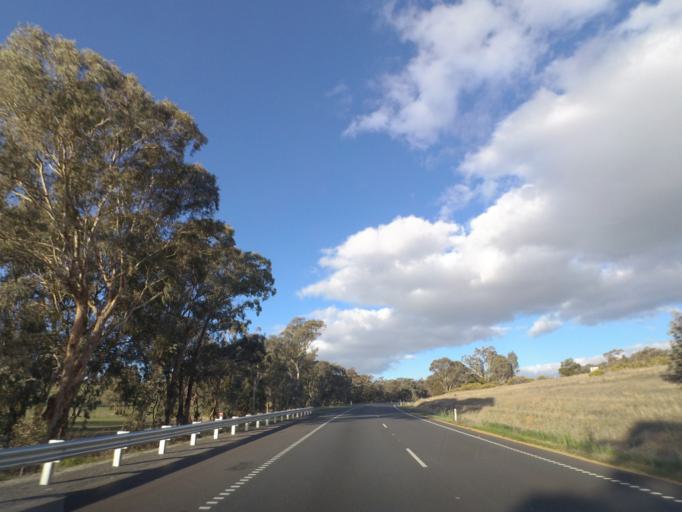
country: AU
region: New South Wales
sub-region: Gundagai
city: Gundagai
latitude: -34.8115
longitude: 148.4193
